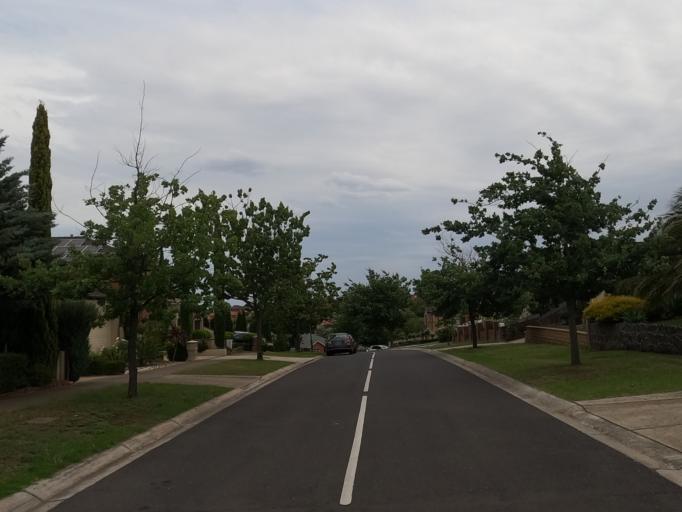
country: AU
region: Victoria
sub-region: Hume
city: Meadow Heights
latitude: -37.6530
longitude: 144.9066
